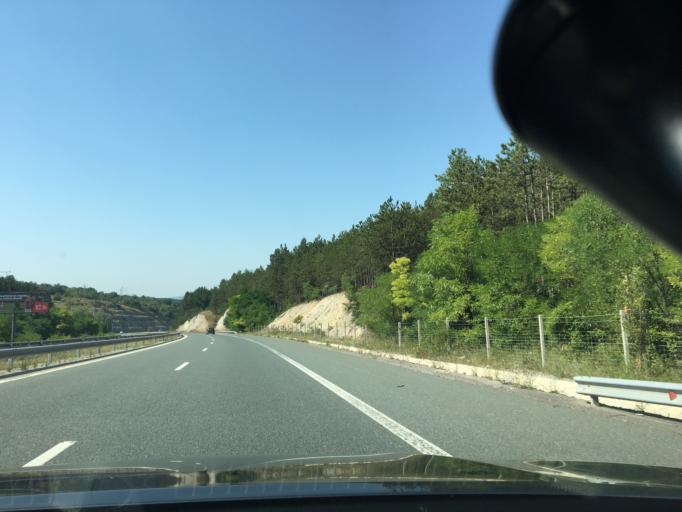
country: BG
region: Pernik
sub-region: Obshtina Pernik
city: Pernik
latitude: 42.4962
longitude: 23.1358
